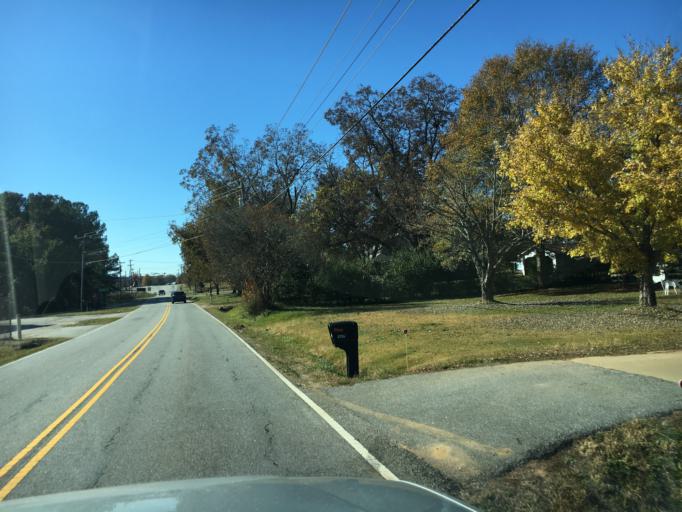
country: US
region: South Carolina
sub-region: Anderson County
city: Centerville
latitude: 34.5119
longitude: -82.7525
